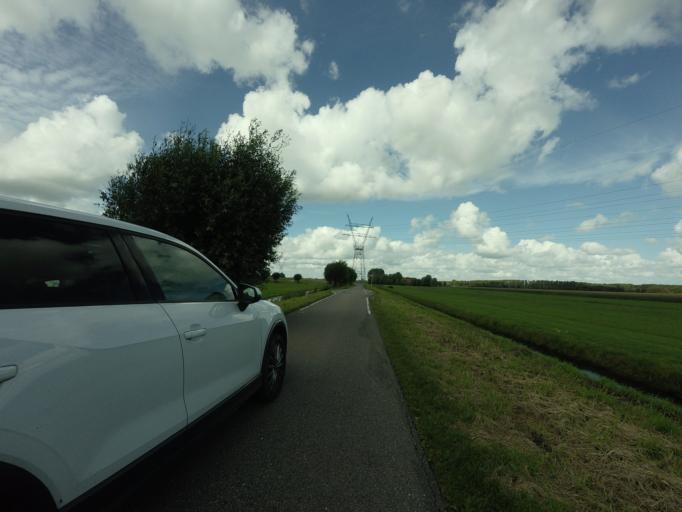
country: NL
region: North Holland
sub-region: Gemeente Purmerend
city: Purmerend
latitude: 52.4650
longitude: 4.9604
